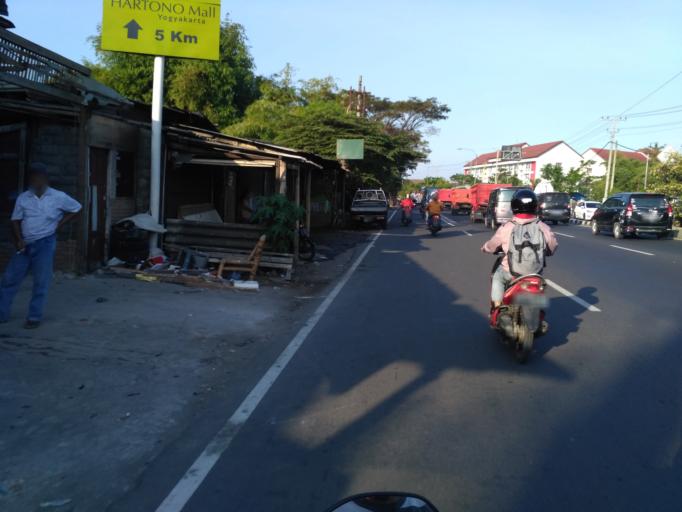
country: ID
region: Daerah Istimewa Yogyakarta
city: Sewon
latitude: -7.8363
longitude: 110.3748
